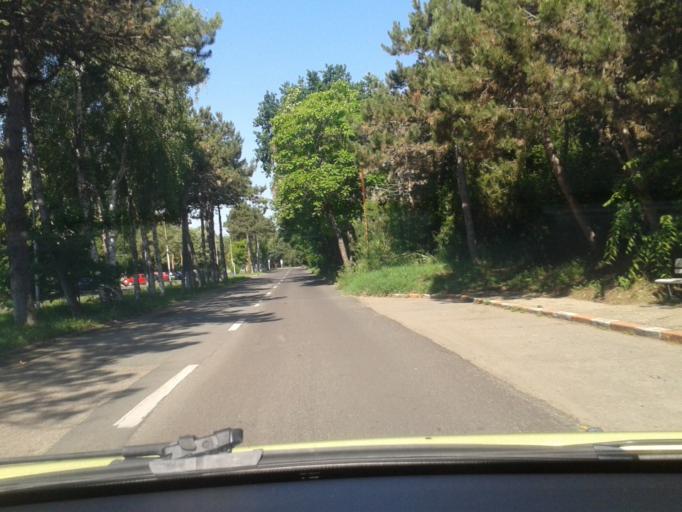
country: RO
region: Constanta
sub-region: Comuna Douazeci si Trei August
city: Douazeci si Trei August
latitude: 43.8753
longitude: 28.6011
